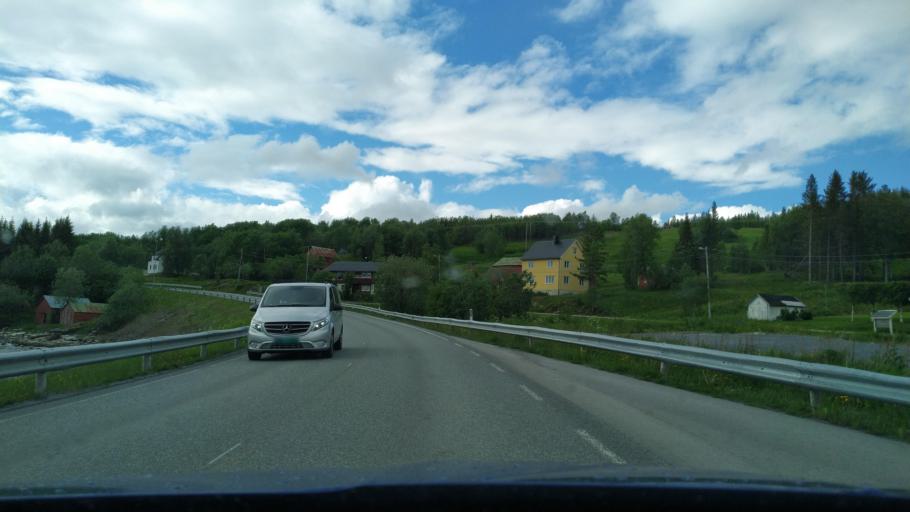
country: NO
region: Troms
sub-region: Sorreisa
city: Sorreisa
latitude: 69.1764
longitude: 18.0823
